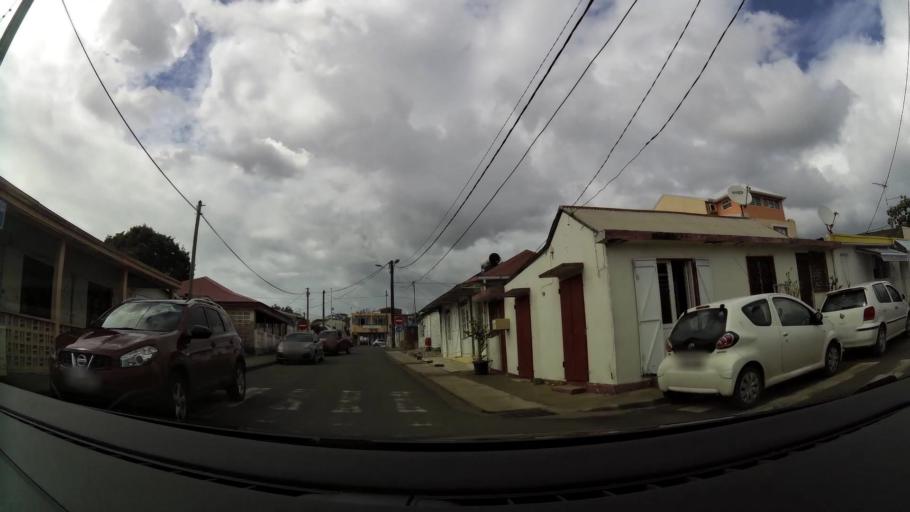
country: GP
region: Guadeloupe
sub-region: Guadeloupe
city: Baie-Mahault
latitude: 16.2666
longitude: -61.5866
